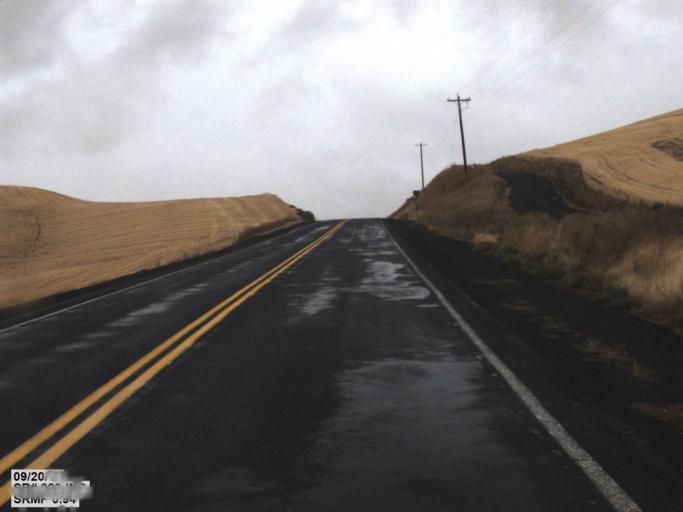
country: US
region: Washington
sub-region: Whitman County
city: Colfax
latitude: 47.0038
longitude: -117.3730
